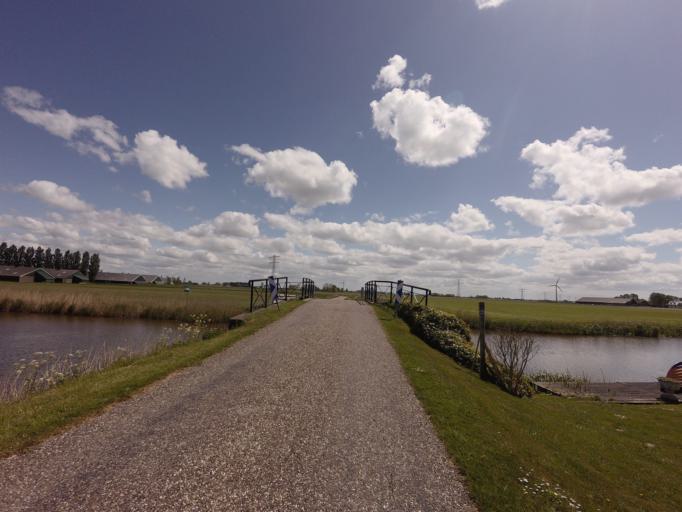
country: NL
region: Friesland
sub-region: Gemeente Franekeradeel
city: Franeker
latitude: 53.1470
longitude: 5.4972
